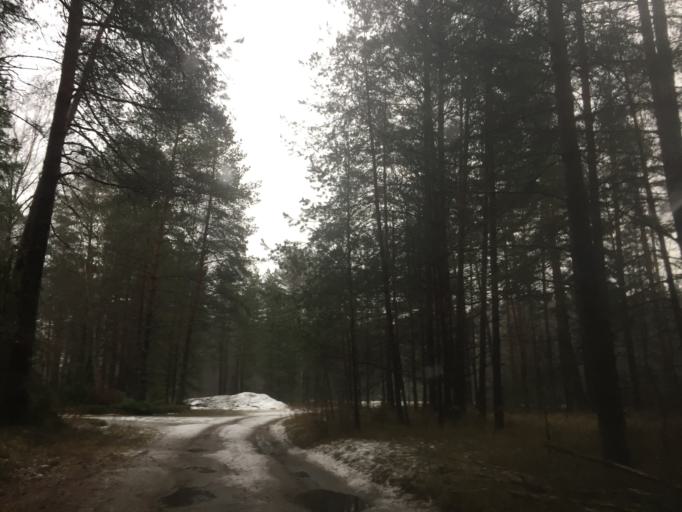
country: LV
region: Stopini
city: Ulbroka
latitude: 56.9477
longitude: 24.3435
